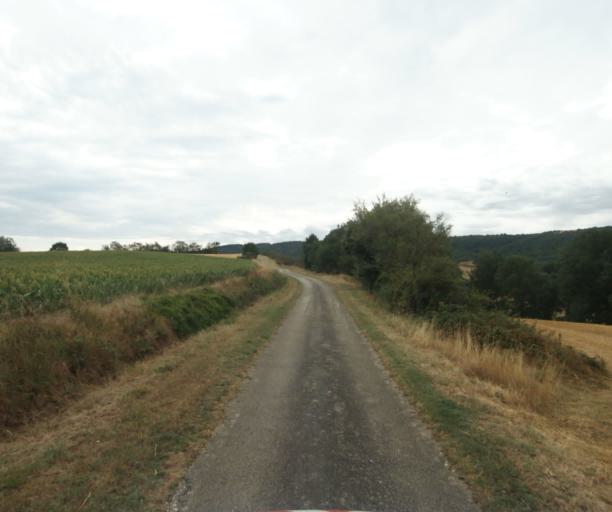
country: FR
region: Midi-Pyrenees
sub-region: Departement de la Haute-Garonne
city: Revel
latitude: 43.4226
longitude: 1.9822
